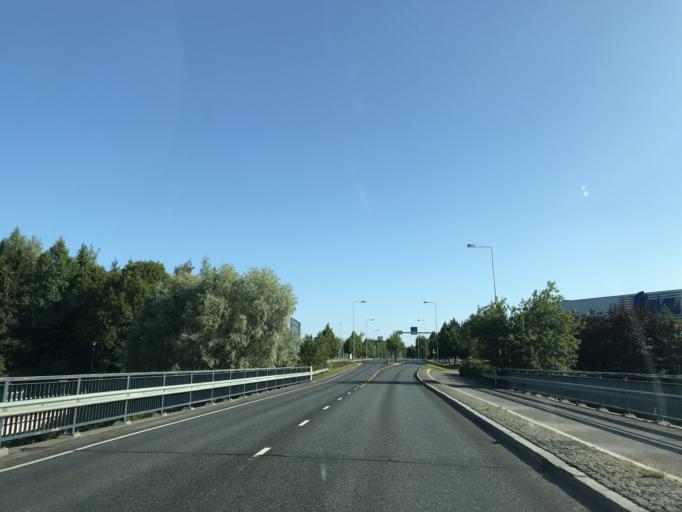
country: FI
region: Paijanne Tavastia
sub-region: Lahti
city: Orimattila
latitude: 60.8040
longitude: 25.7287
